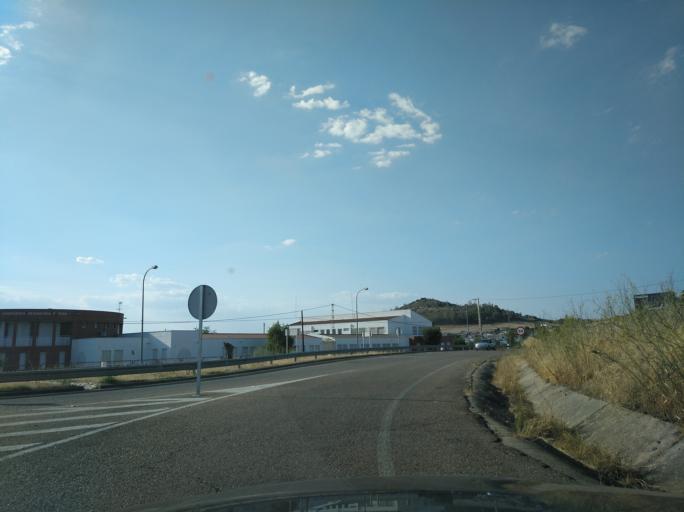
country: ES
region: Extremadura
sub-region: Provincia de Badajoz
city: Alconchel
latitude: 38.5097
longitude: -7.0699
